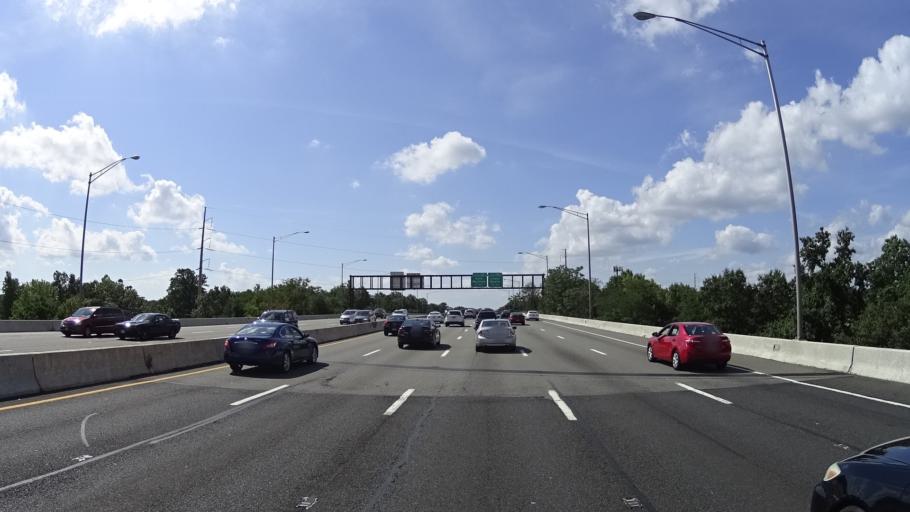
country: US
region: New Jersey
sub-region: Union County
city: Cranford
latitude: 40.6560
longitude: -74.2874
